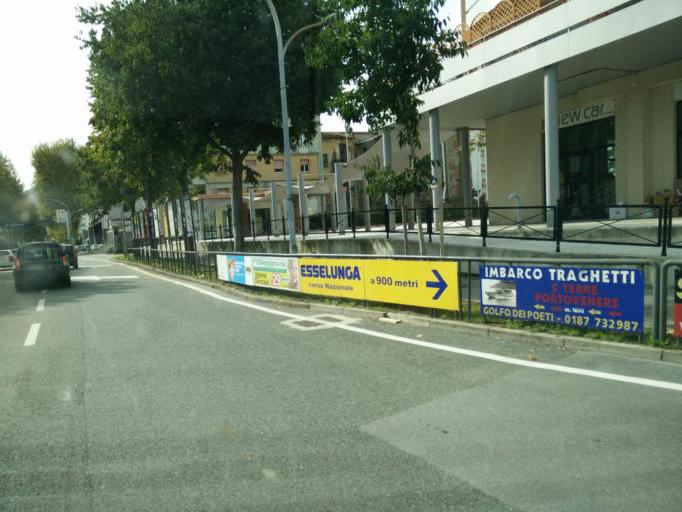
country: IT
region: Liguria
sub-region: Provincia di La Spezia
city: La Spezia
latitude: 44.1140
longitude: 9.8382
